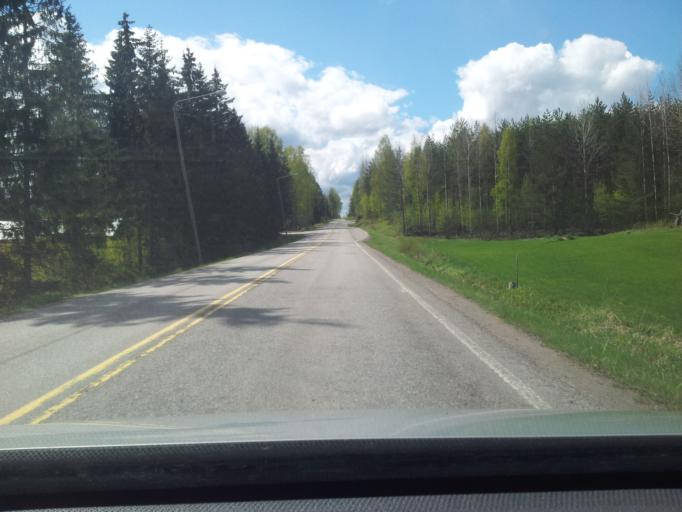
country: FI
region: Uusimaa
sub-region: Loviisa
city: Perna
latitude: 60.4999
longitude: 25.9207
